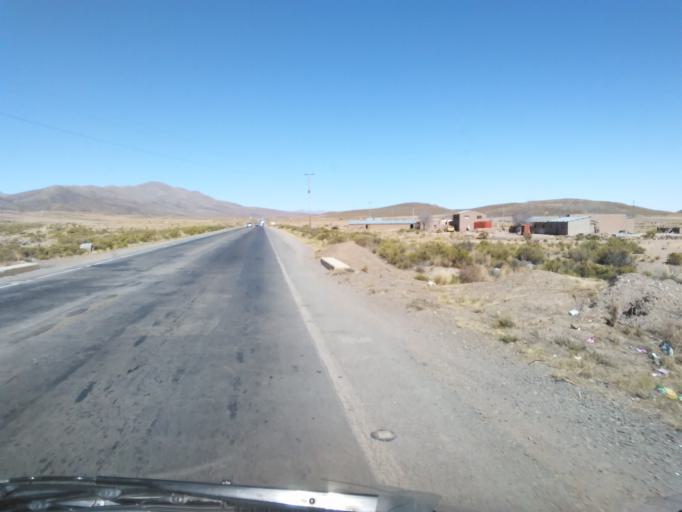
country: BO
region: Oruro
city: Machacamarca
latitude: -18.0332
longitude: -67.0194
